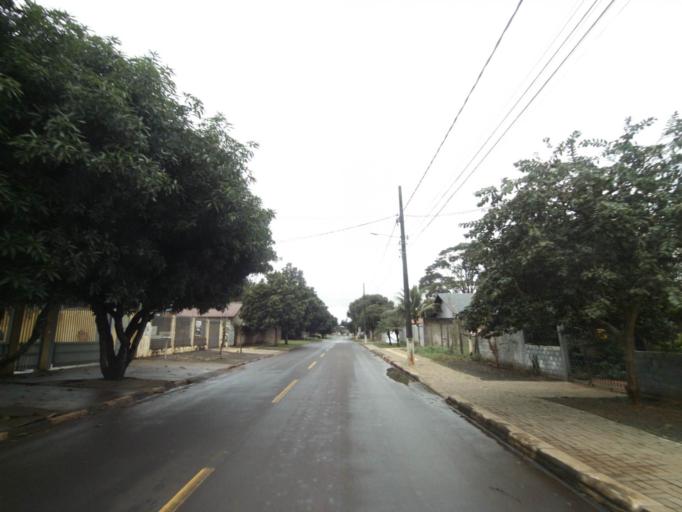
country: BR
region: Parana
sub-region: Foz Do Iguacu
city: Foz do Iguacu
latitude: -25.5141
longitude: -54.5603
